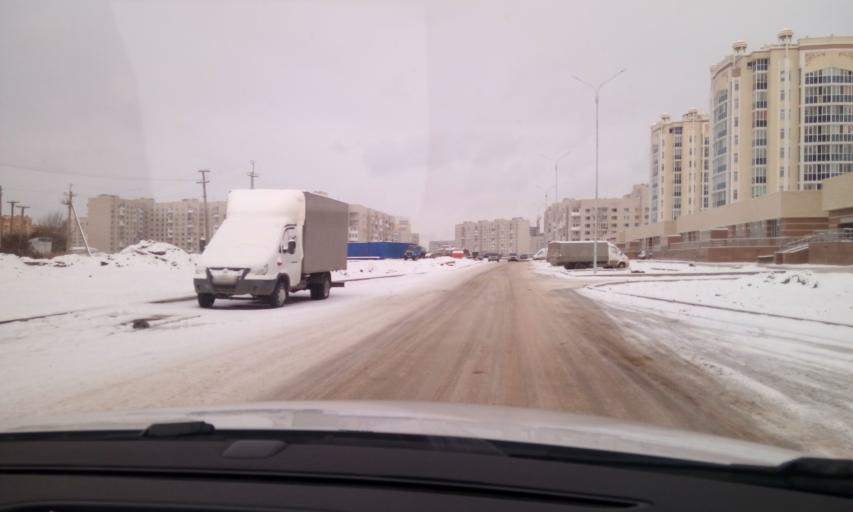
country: KZ
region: Astana Qalasy
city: Astana
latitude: 51.1201
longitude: 71.5036
